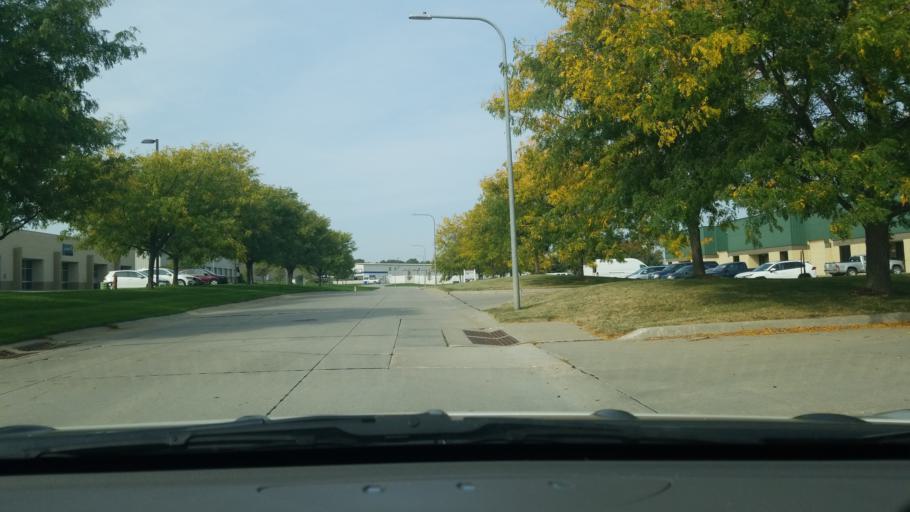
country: US
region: Nebraska
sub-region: Sarpy County
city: Chalco
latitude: 41.1724
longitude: -96.1206
